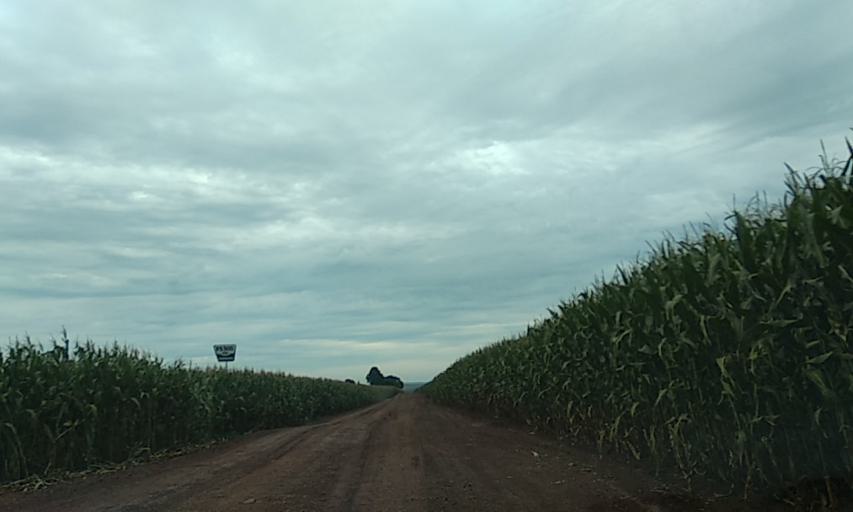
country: BR
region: Parana
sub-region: Marechal Candido Rondon
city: Marechal Candido Rondon
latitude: -24.5397
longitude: -54.0940
